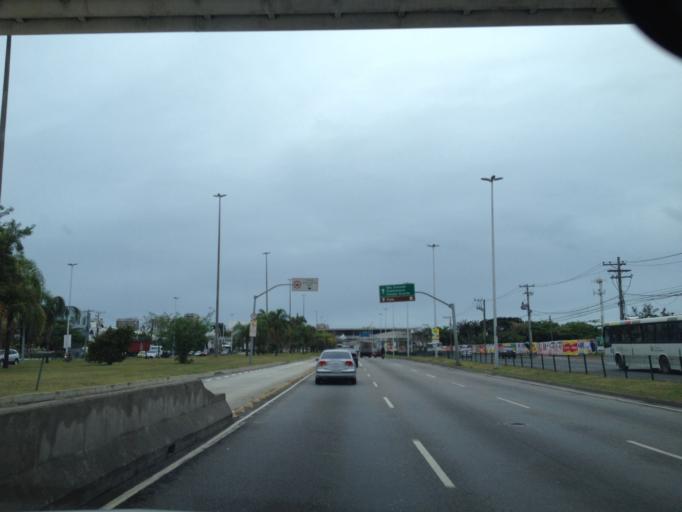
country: BR
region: Rio de Janeiro
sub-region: Rio De Janeiro
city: Rio de Janeiro
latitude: -22.9889
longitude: -43.3660
